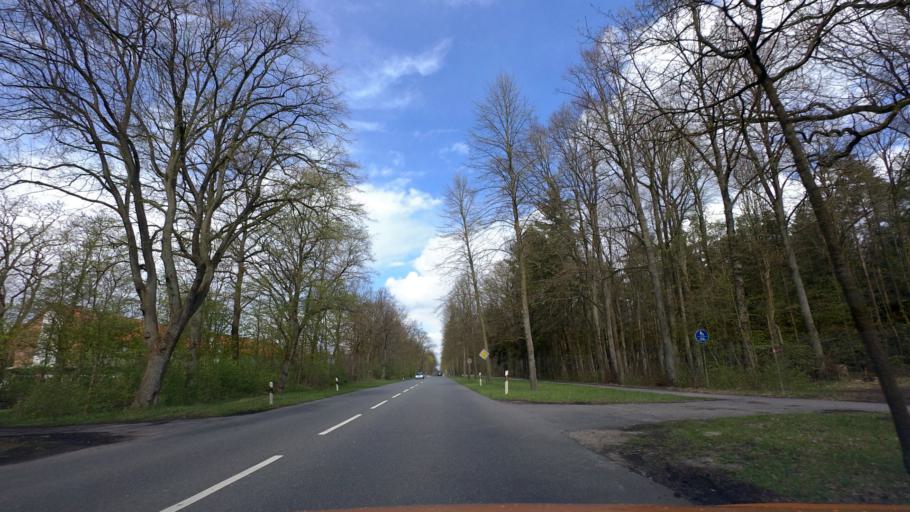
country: DE
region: Lower Saxony
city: Deutsch Evern
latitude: 53.2178
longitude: 10.4056
